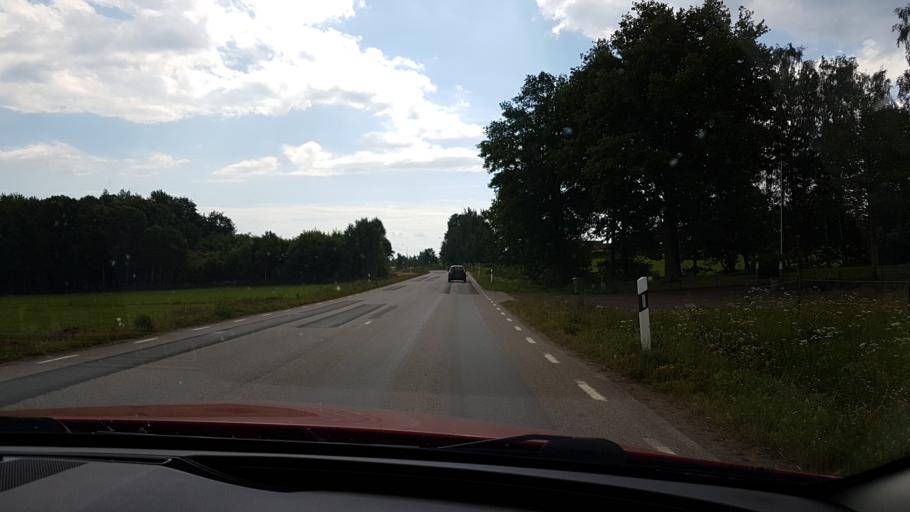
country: SE
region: Vaestra Goetaland
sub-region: Hjo Kommun
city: Hjo
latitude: 58.3051
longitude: 14.2493
